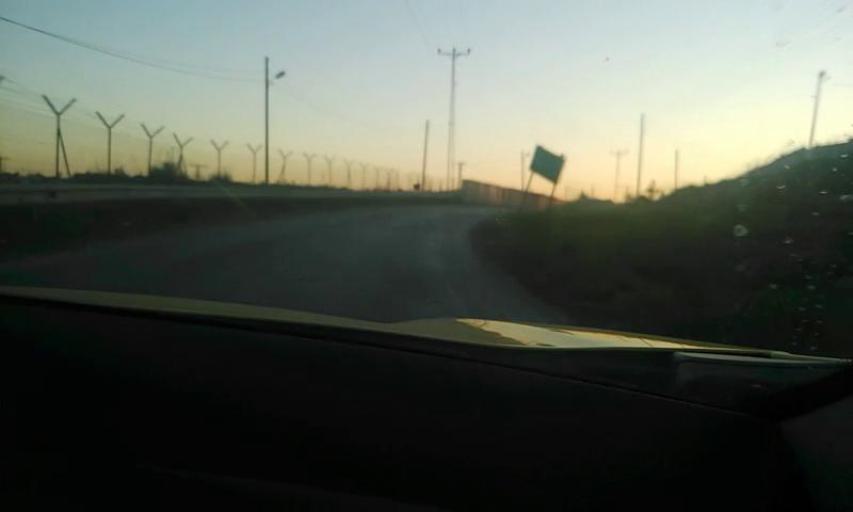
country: PS
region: West Bank
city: Silwad
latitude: 31.9607
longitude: 35.2618
